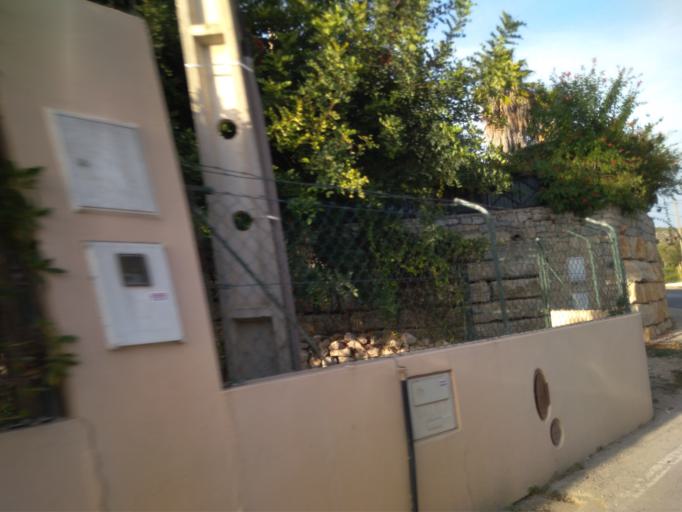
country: PT
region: Faro
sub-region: Faro
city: Santa Barbara de Nexe
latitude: 37.1032
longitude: -7.9602
